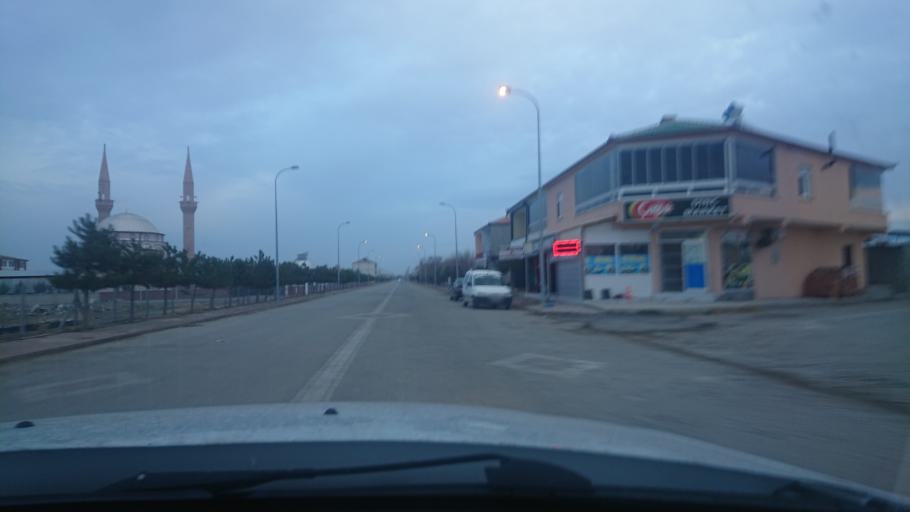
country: TR
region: Aksaray
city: Yesilova
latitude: 38.3324
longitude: 33.7519
